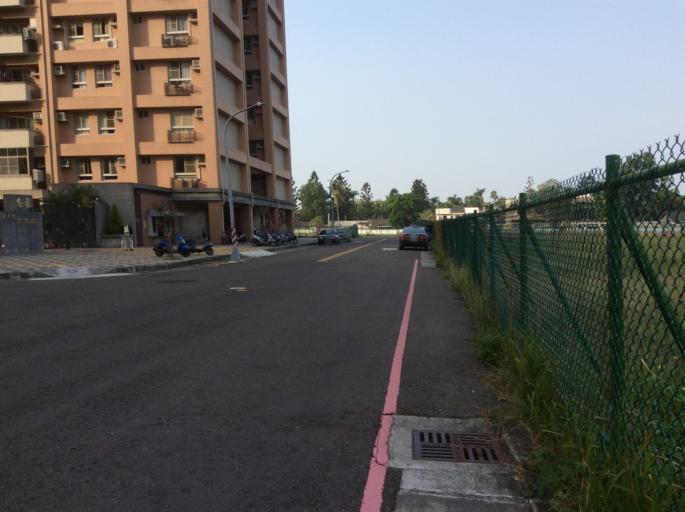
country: TW
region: Kaohsiung
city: Kaohsiung
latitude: 22.6983
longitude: 120.2877
